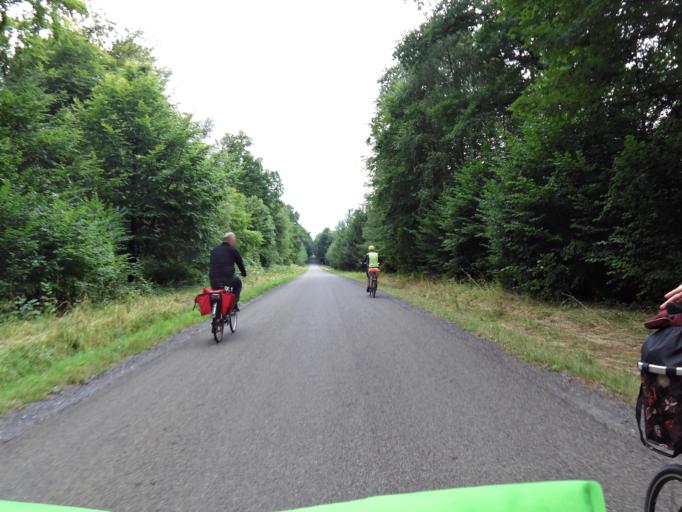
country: BE
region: Wallonia
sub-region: Province de Namur
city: Bievre
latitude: 49.9224
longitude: 5.0048
